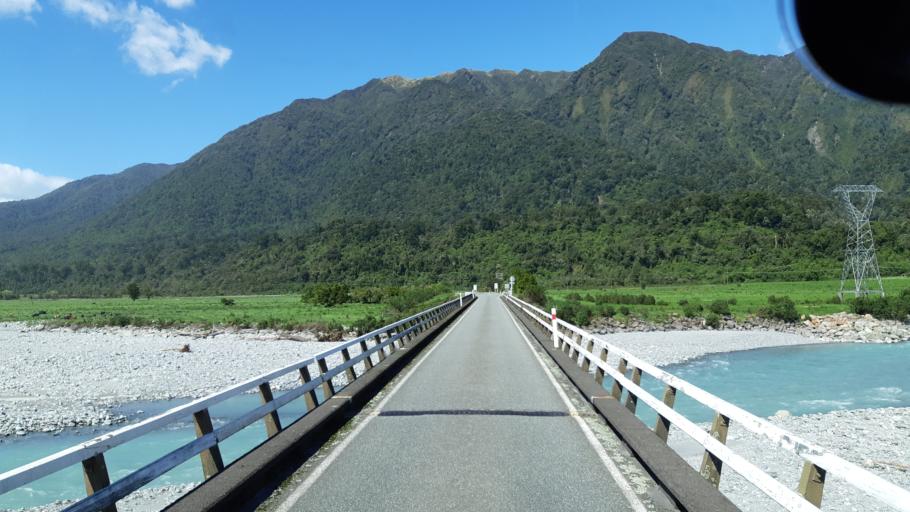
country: NZ
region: West Coast
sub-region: Westland District
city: Hokitika
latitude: -43.1554
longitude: 170.6238
